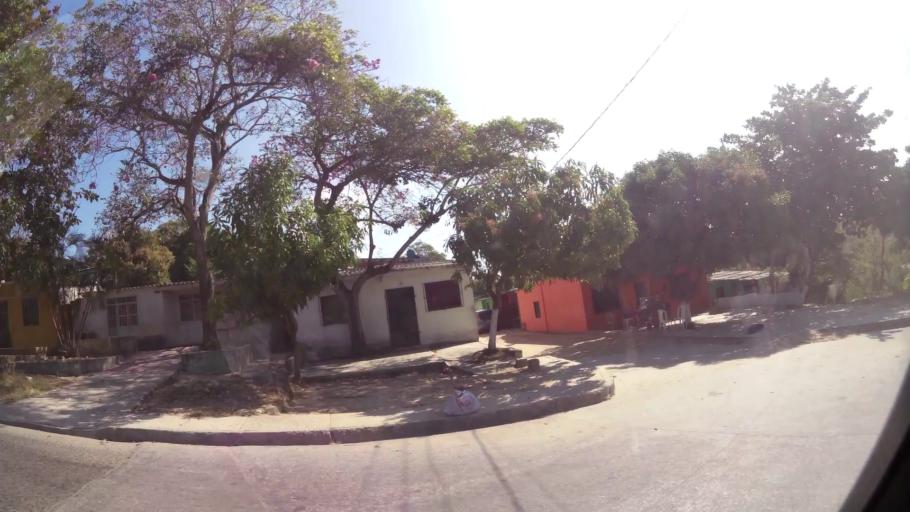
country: CO
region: Atlantico
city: Barranquilla
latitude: 10.9834
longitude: -74.8248
